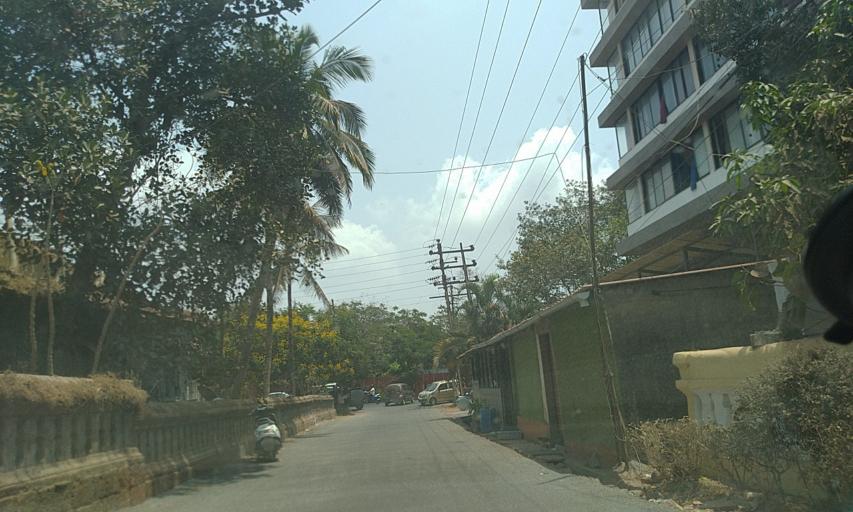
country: IN
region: Goa
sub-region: North Goa
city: Serula
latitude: 15.5401
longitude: 73.8214
